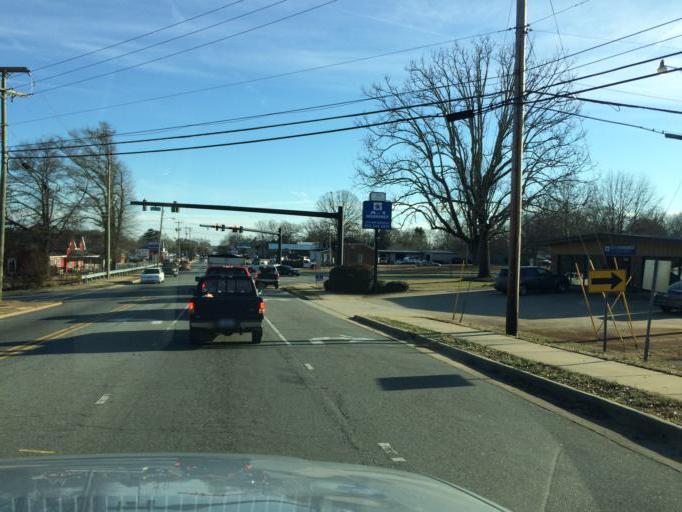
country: US
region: North Carolina
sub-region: Rutherford County
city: Forest City
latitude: 35.3283
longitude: -81.8625
